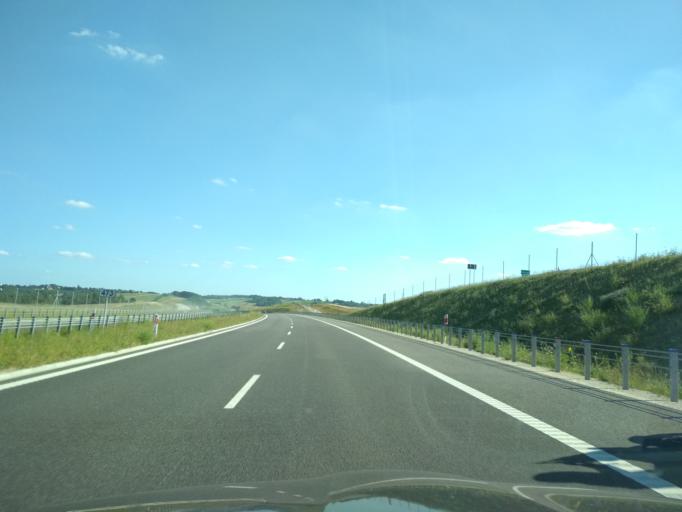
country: PL
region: Subcarpathian Voivodeship
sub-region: Rzeszow
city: Przybyszowka
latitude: 50.0577
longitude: 21.9236
